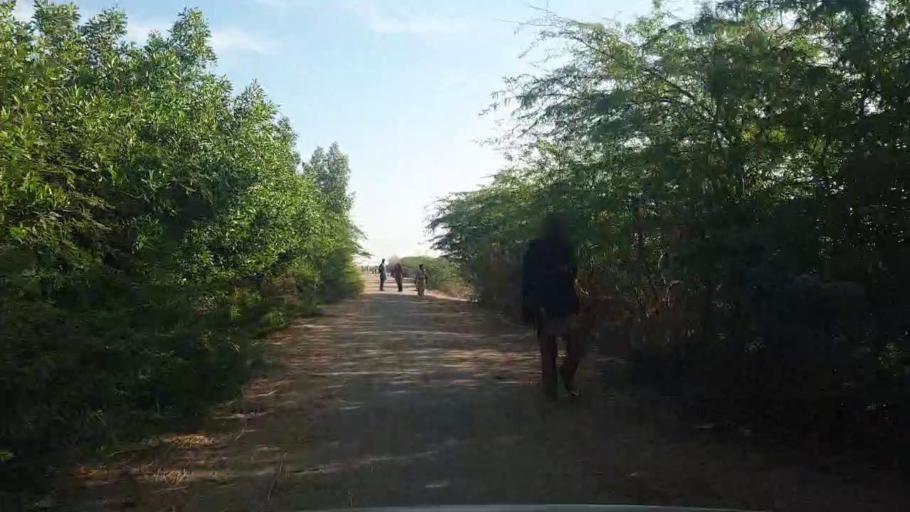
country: PK
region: Sindh
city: Talhar
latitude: 24.8361
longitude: 68.8435
